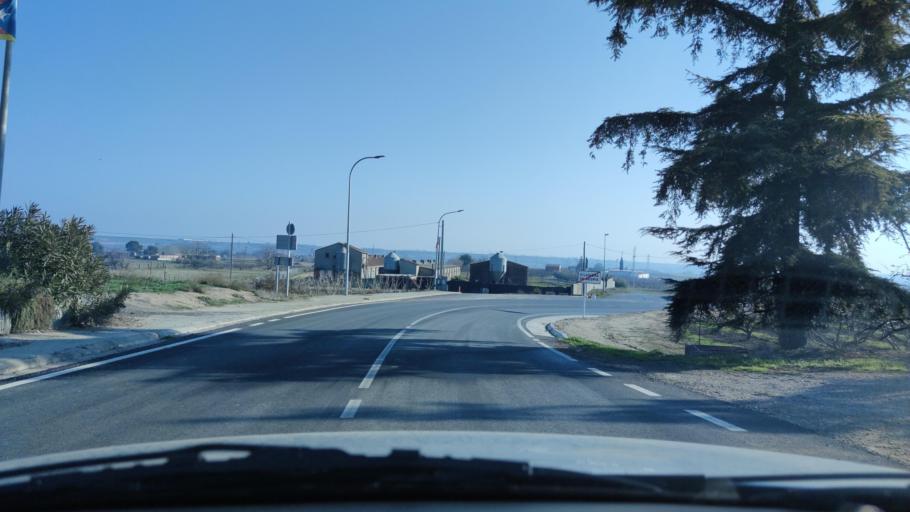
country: ES
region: Catalonia
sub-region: Provincia de Lleida
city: Torrefarrera
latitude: 41.7107
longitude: 0.6223
